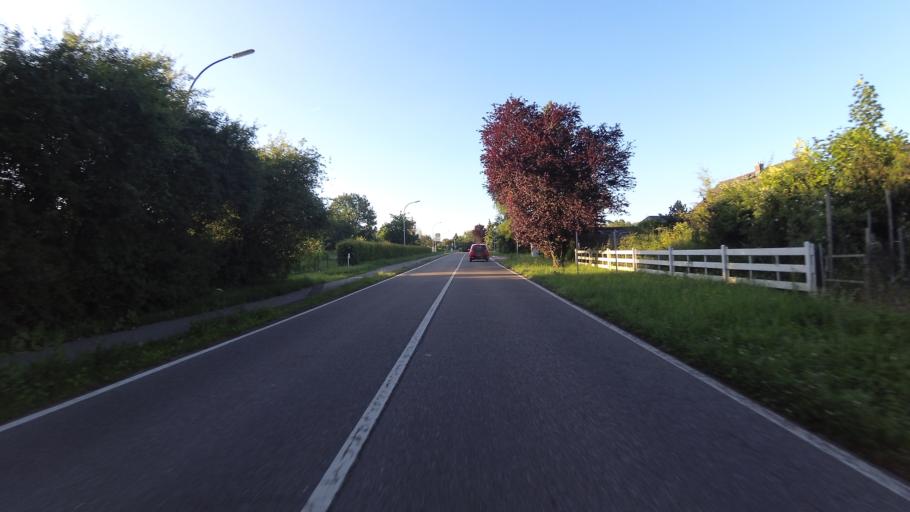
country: FR
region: Lorraine
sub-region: Departement de la Moselle
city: Sarreguemines
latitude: 49.1282
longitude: 7.0670
